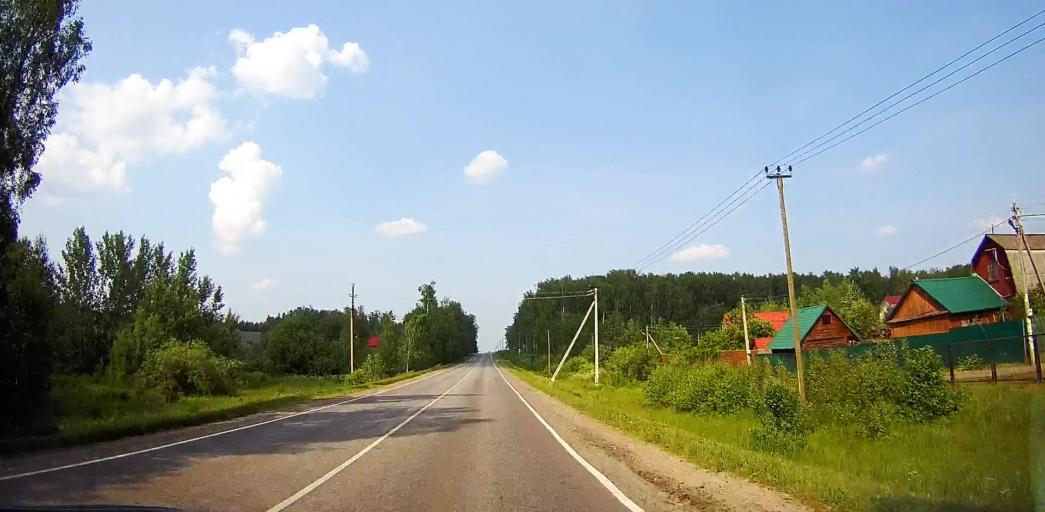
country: RU
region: Moskovskaya
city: Mikhnevo
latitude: 55.1673
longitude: 37.9598
